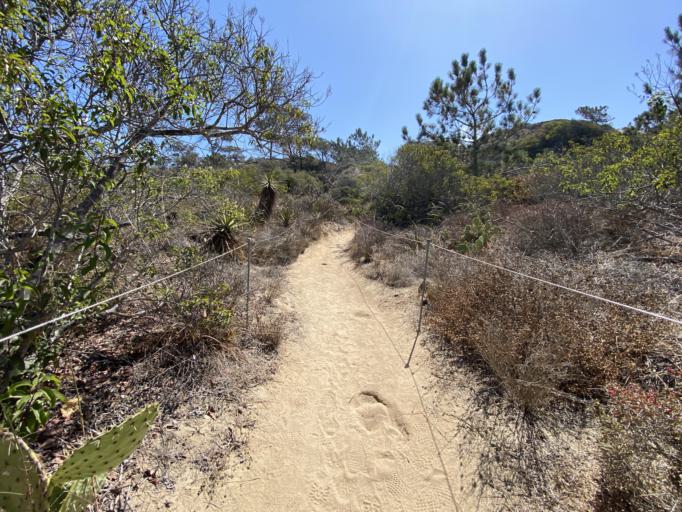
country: US
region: California
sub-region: San Diego County
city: Del Mar
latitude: 32.9213
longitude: -117.2566
